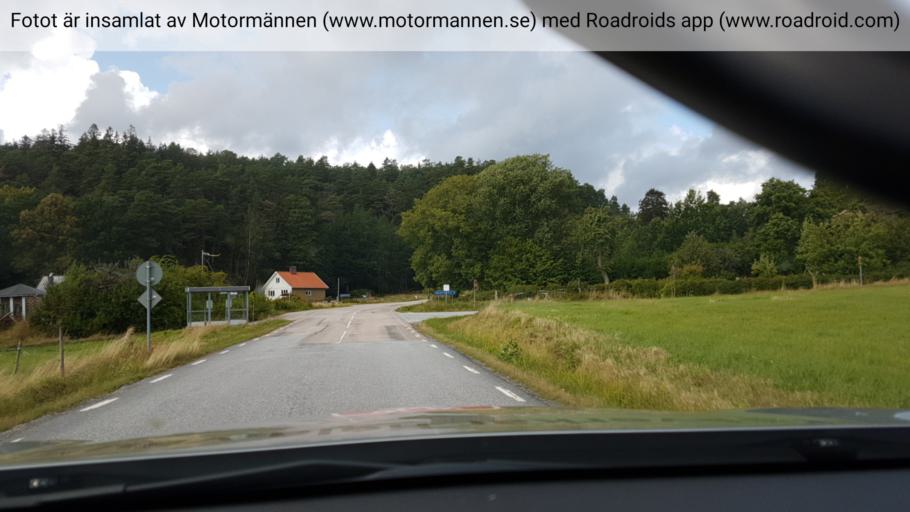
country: SE
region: Vaestra Goetaland
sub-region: Uddevalla Kommun
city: Ljungskile
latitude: 58.2592
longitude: 11.8525
